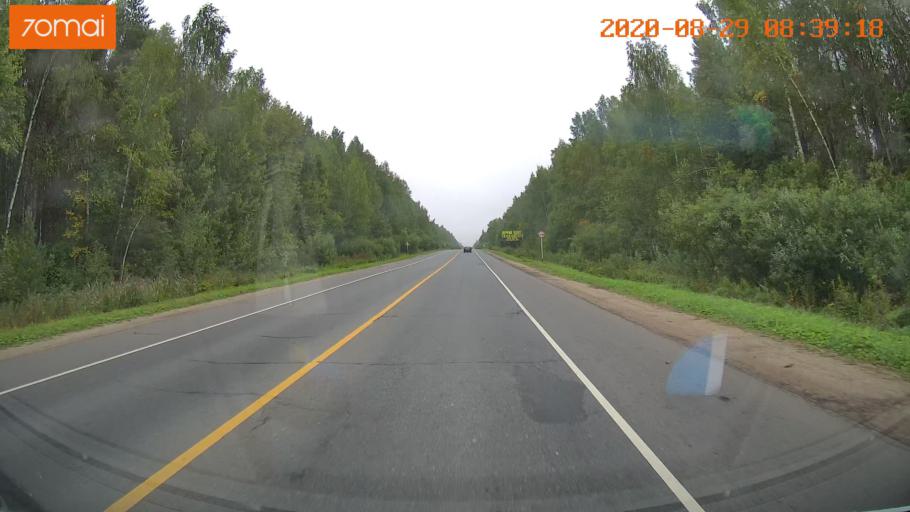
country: RU
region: Ivanovo
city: Rodniki
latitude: 57.0881
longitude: 41.6946
